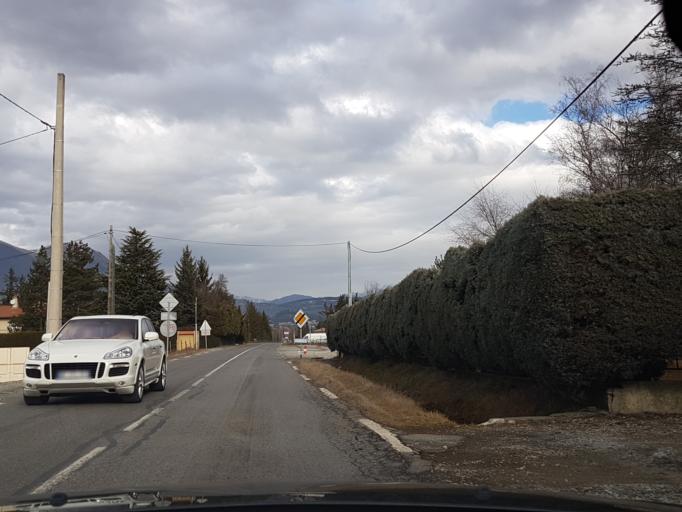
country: FR
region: Provence-Alpes-Cote d'Azur
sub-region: Departement des Hautes-Alpes
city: Gap
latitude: 44.5275
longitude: 6.0598
